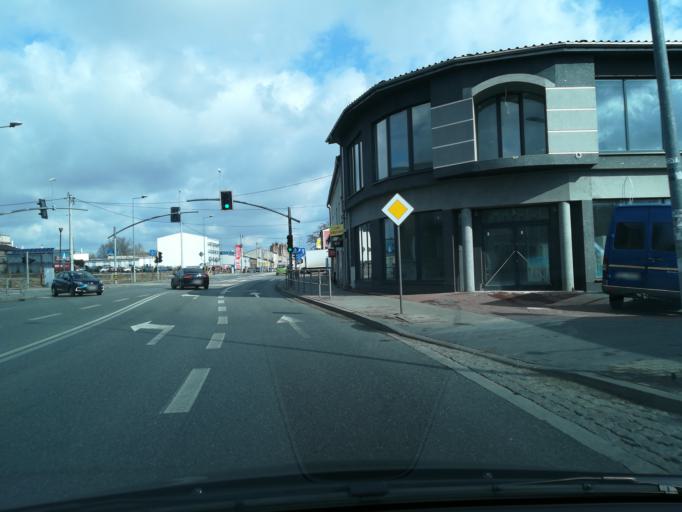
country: PL
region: Silesian Voivodeship
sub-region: Czestochowa
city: Czestochowa
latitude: 50.8183
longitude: 19.1300
